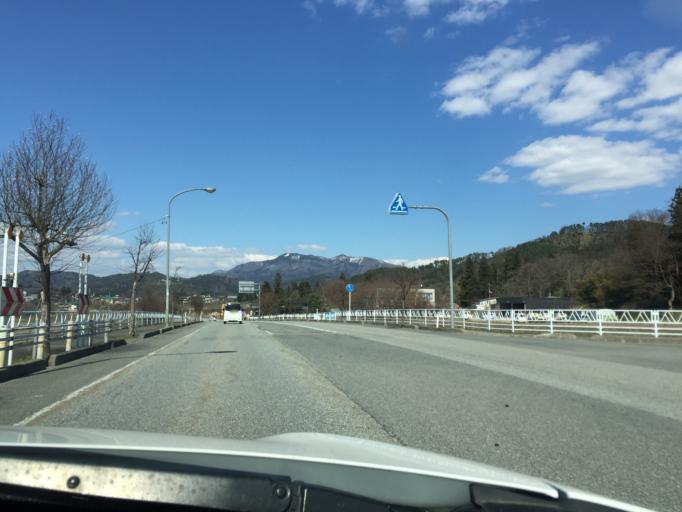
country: JP
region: Yamagata
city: Nagai
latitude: 38.1712
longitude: 140.0899
